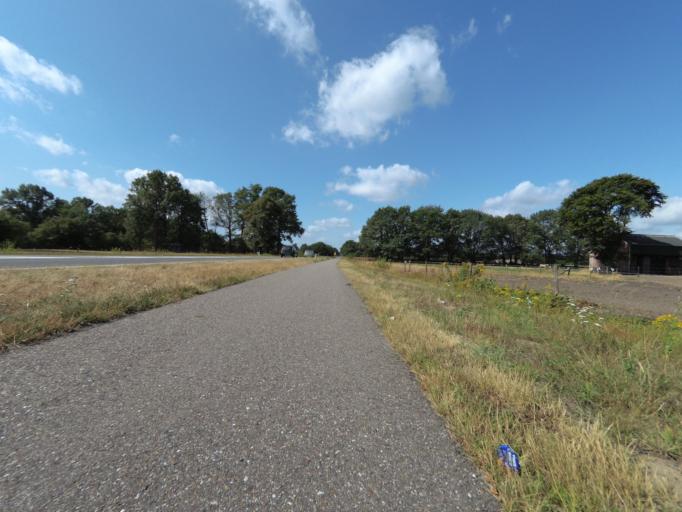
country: NL
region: Overijssel
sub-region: Gemeente Oldenzaal
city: Oldenzaal
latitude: 52.2944
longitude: 6.8783
